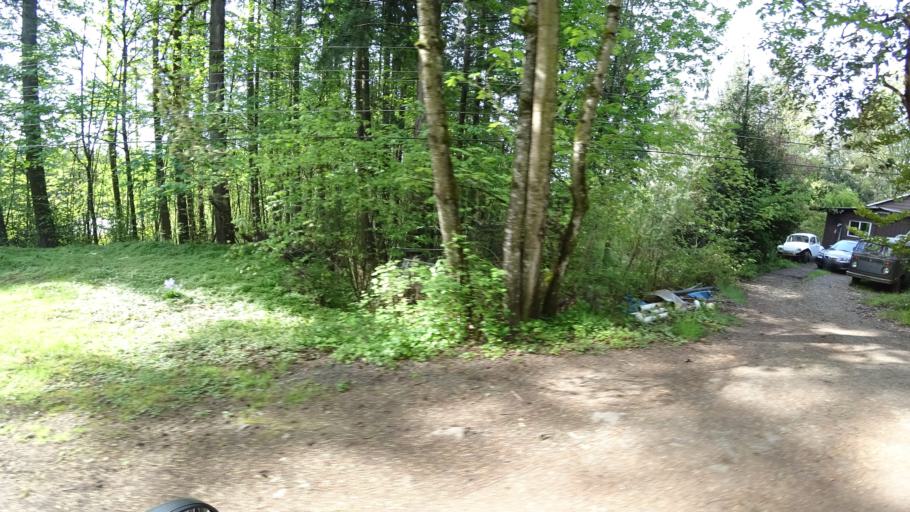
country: US
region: Oregon
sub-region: Washington County
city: Aloha
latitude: 45.4368
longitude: -122.8534
